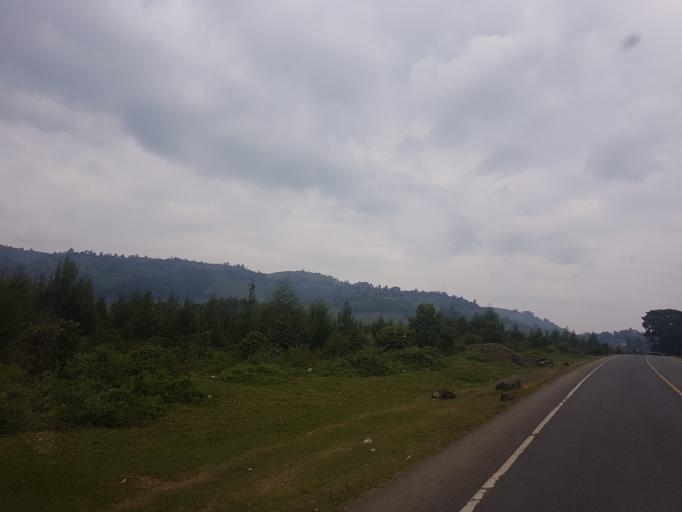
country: UG
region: Western Region
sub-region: Kisoro District
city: Kisoro
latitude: -1.2101
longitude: 29.8248
